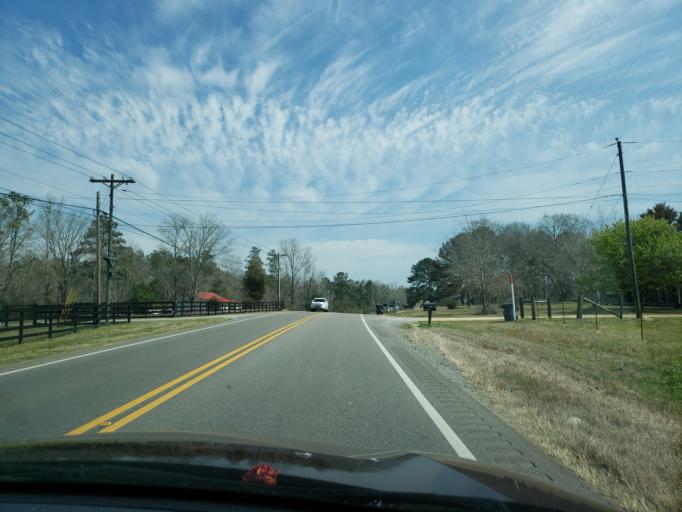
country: US
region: Alabama
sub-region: Elmore County
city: Eclectic
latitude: 32.5813
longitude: -86.0795
